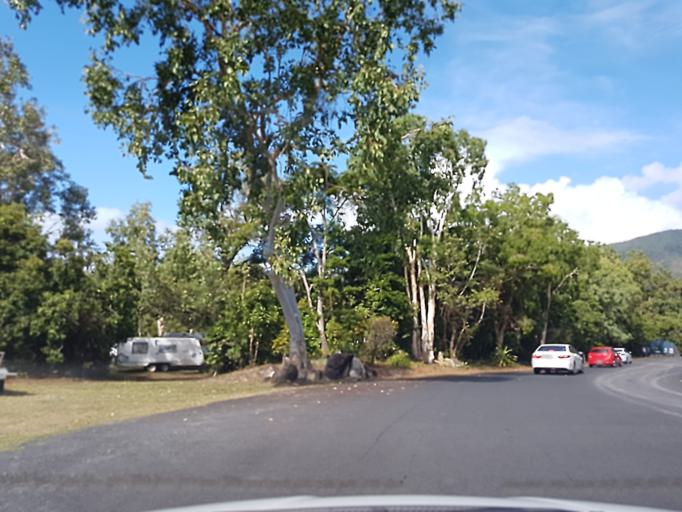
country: AU
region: Queensland
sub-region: Cairns
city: Palm Cove
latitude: -16.6619
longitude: 145.5656
